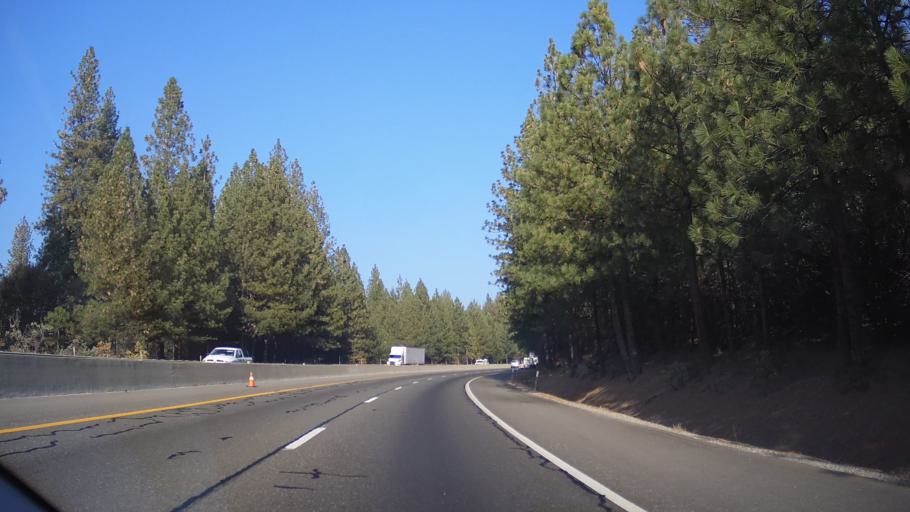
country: US
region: California
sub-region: Placer County
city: Colfax
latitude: 39.1687
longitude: -120.8743
